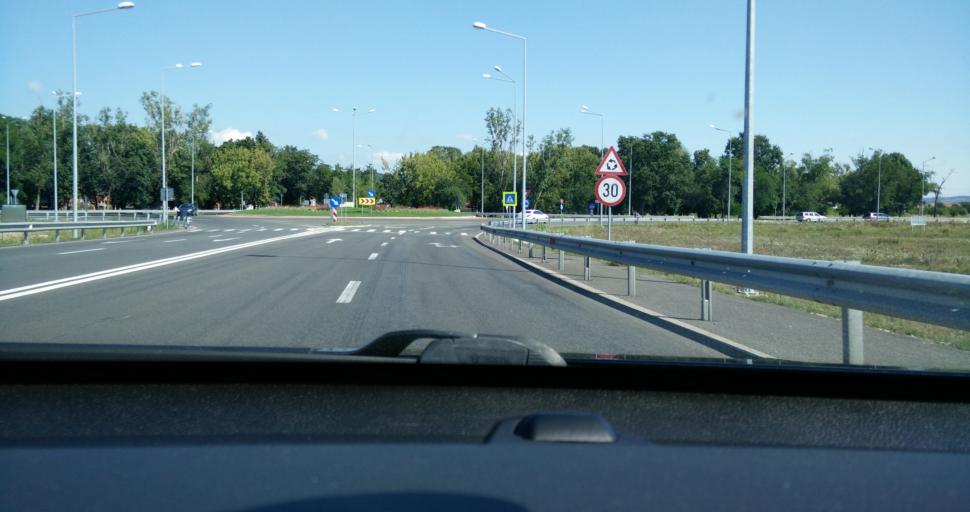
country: RO
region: Bihor
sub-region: Comuna Sanmartin
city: Sanmartin
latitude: 47.0357
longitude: 21.9963
